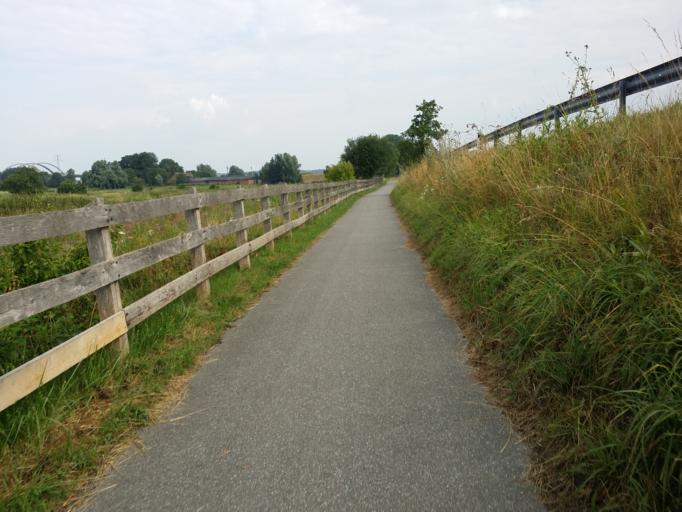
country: DE
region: Schleswig-Holstein
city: Heiligenstedten
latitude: 53.9173
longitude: 9.4885
